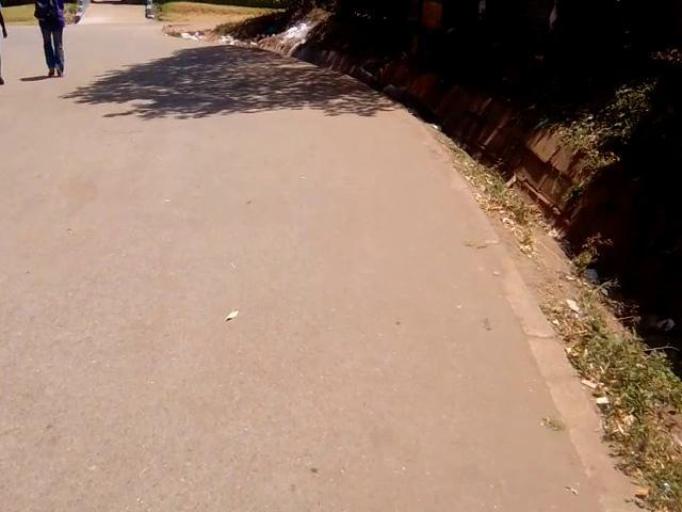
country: KE
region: Nairobi Area
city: Nairobi
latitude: -1.3143
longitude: 36.7760
